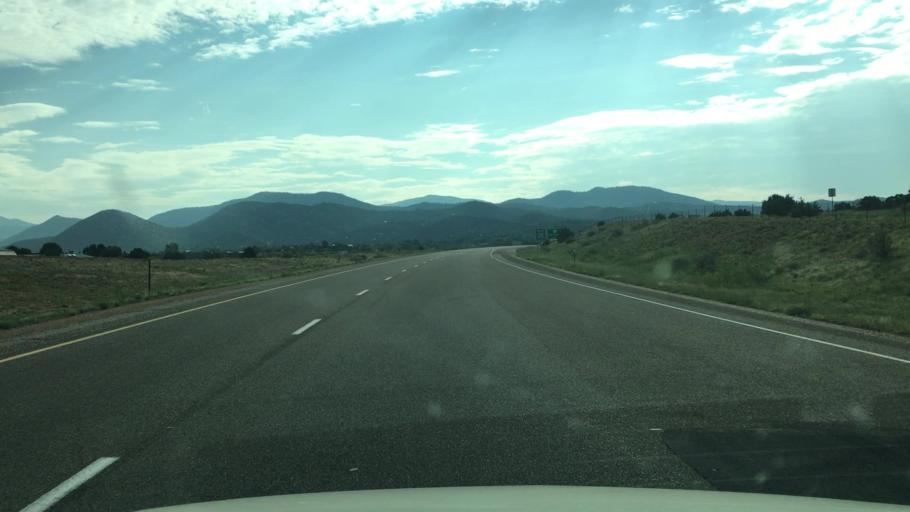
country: US
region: New Mexico
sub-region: Santa Fe County
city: Santa Fe
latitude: 35.6362
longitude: -105.9506
